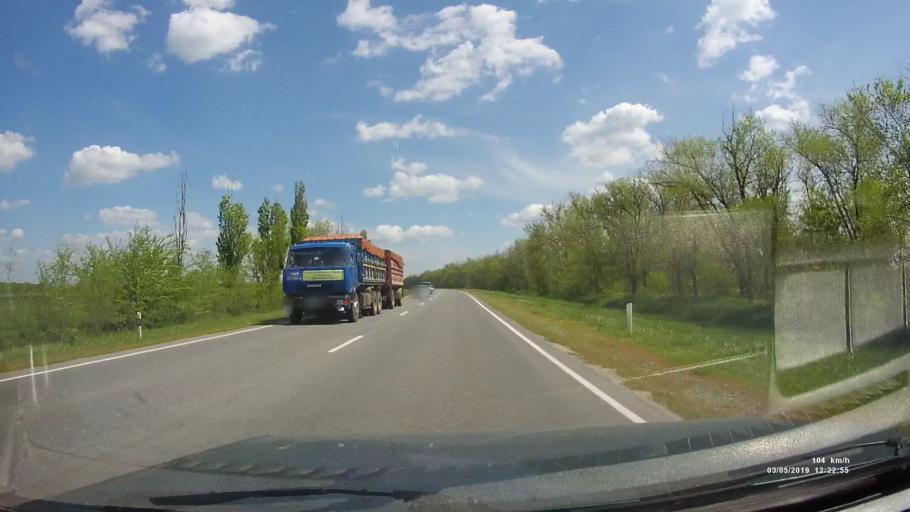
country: RU
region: Rostov
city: Semikarakorsk
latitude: 47.4067
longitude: 40.6721
